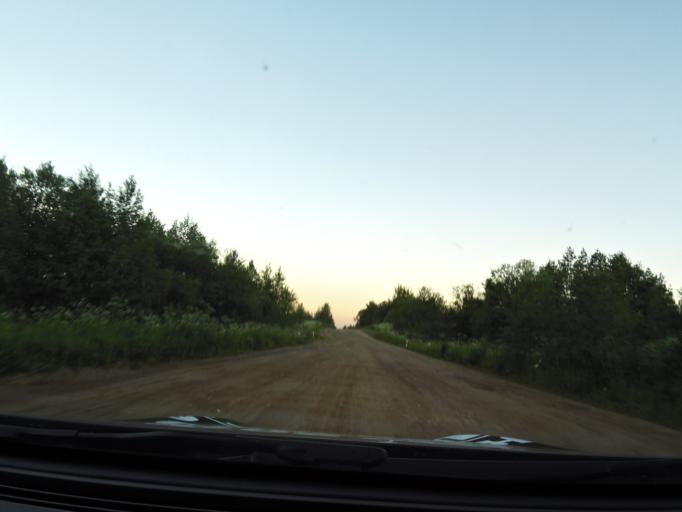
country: RU
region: Leningrad
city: Voznesen'ye
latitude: 60.8736
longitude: 35.5239
